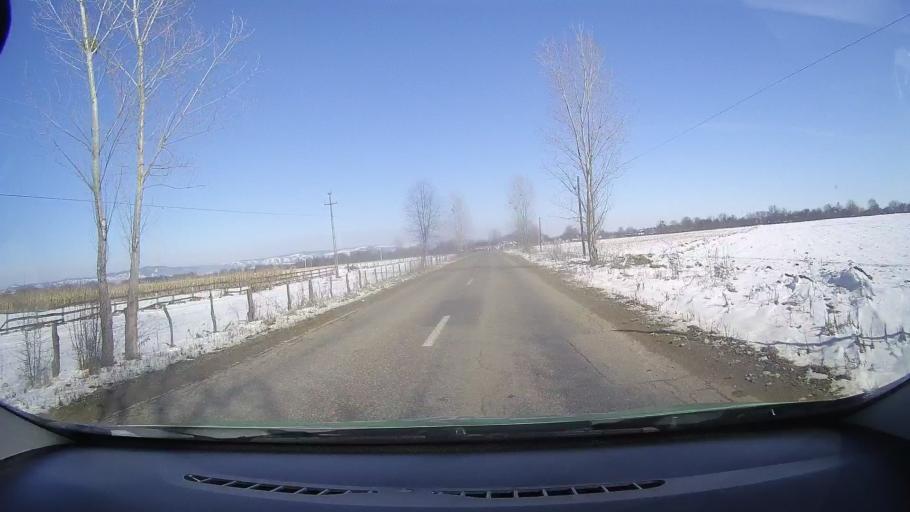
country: RO
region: Brasov
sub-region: Oras Victoria
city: Victoria
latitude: 45.7391
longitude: 24.7347
